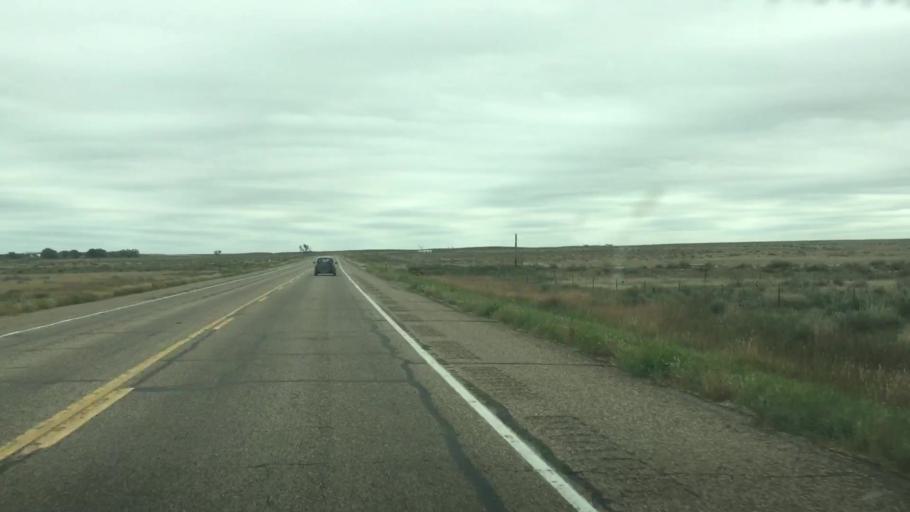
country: US
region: Colorado
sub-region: Prowers County
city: Lamar
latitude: 38.0574
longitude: -102.2835
